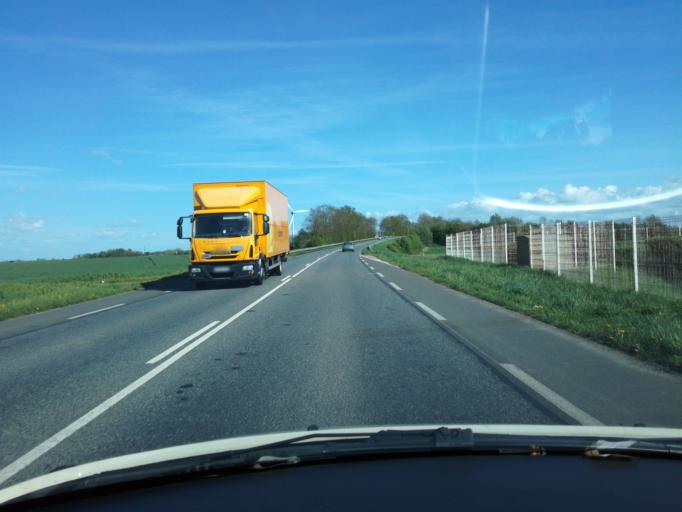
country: FR
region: Picardie
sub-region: Departement de la Somme
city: Feuquieres-en-Vimeu
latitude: 50.0678
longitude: 1.6125
